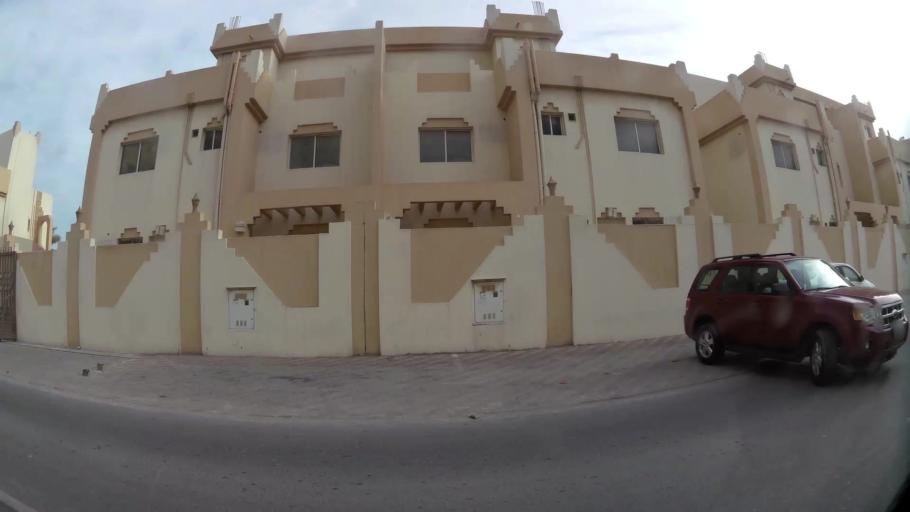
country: QA
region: Baladiyat ad Dawhah
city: Doha
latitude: 25.2793
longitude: 51.4961
